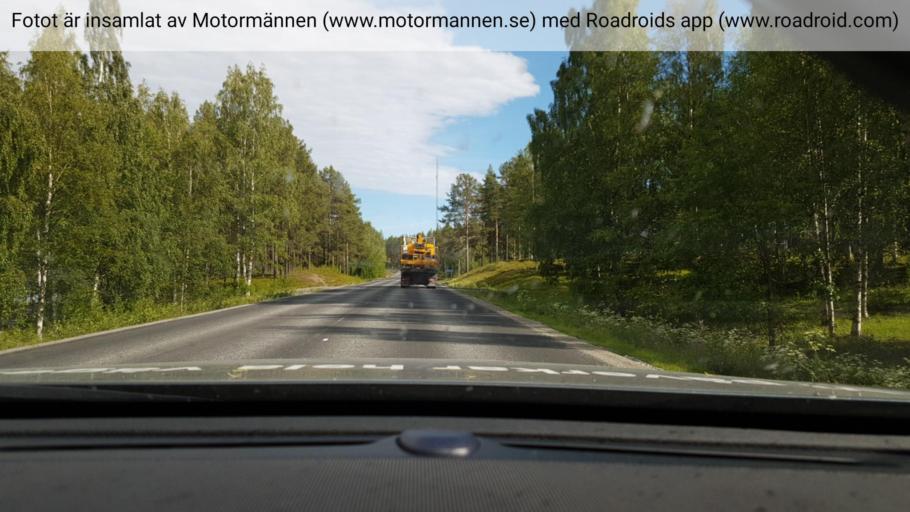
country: SE
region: Vaesterbotten
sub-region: Lycksele Kommun
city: Soderfors
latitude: 64.8340
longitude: 18.0027
